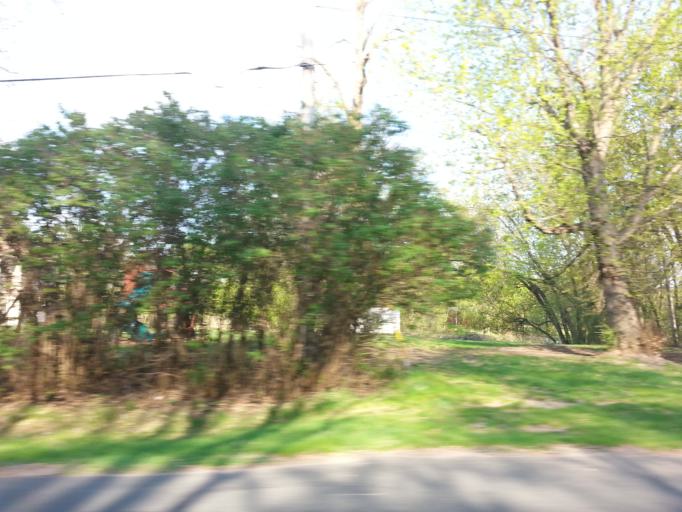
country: US
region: Minnesota
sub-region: Washington County
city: Lake Elmo
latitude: 44.9915
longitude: -92.8431
